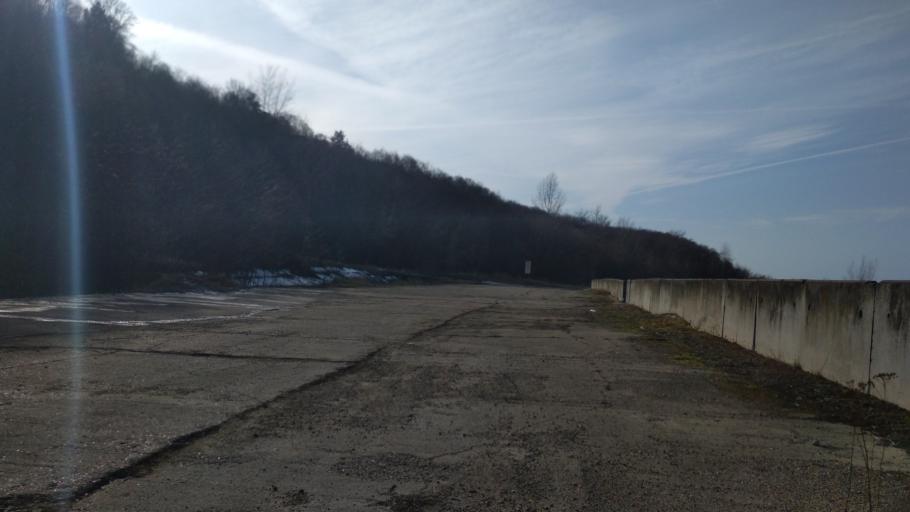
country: RU
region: Chuvashia
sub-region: Cheboksarskiy Rayon
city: Cheboksary
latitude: 56.1442
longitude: 47.3254
